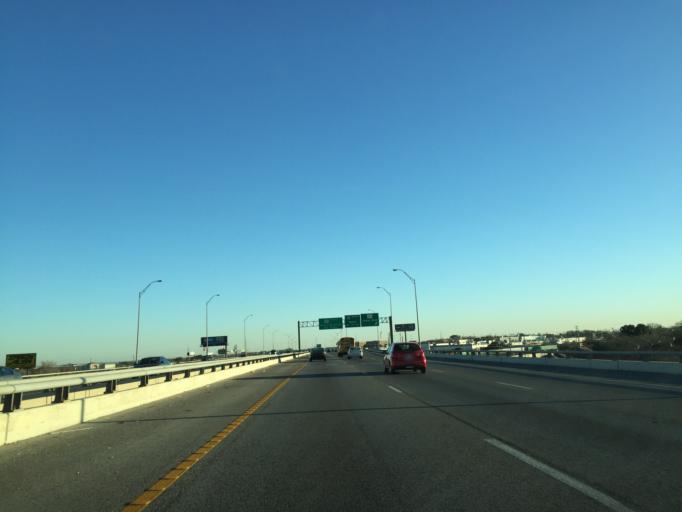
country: US
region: Texas
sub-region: Travis County
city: Austin
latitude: 30.3560
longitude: -97.7155
